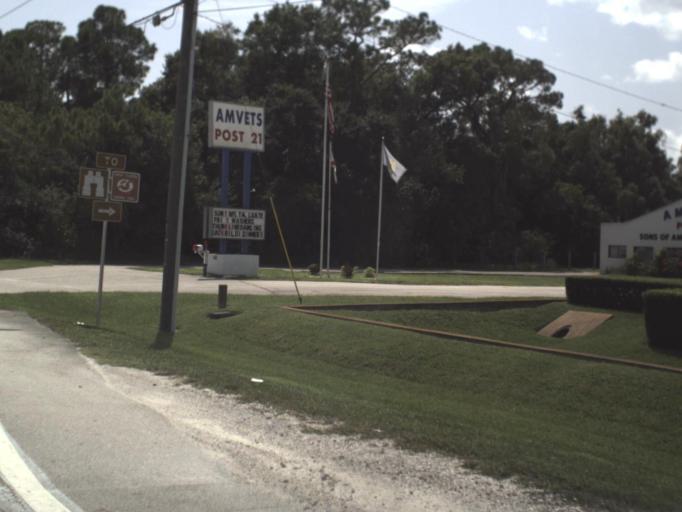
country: US
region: Florida
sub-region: Highlands County
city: Sebring
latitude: 27.4769
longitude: -81.4743
